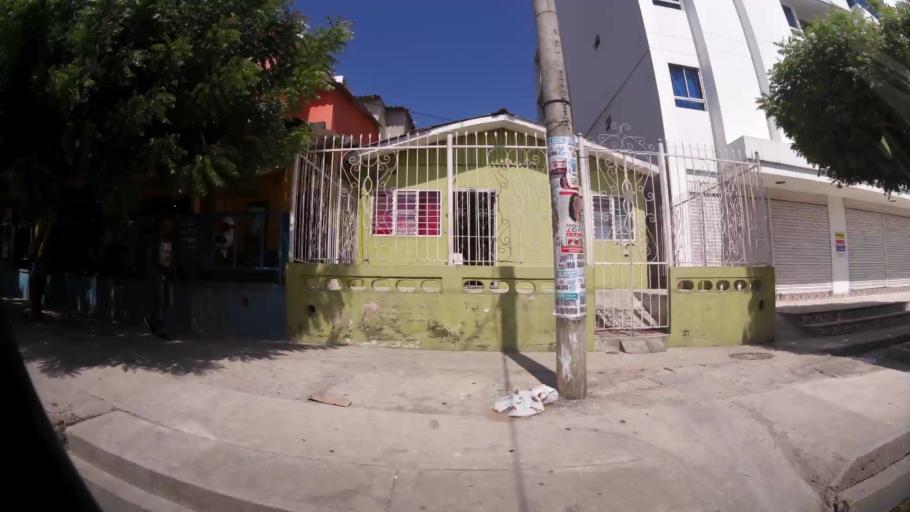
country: CO
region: Atlantico
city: Barranquilla
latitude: 10.9686
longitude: -74.8023
